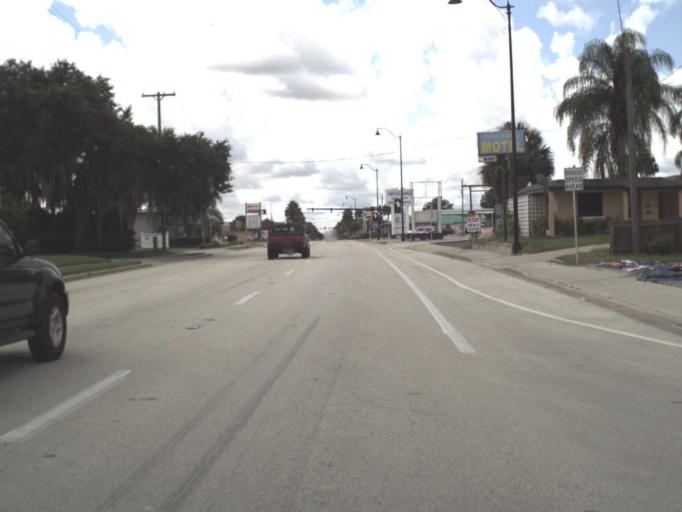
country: US
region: Florida
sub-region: Hardee County
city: Wauchula
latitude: 27.5520
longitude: -81.8129
